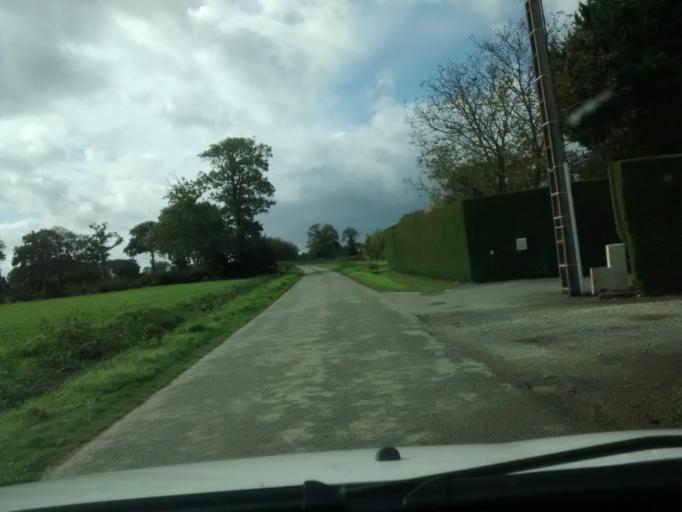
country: FR
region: Brittany
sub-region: Departement d'Ille-et-Vilaine
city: Montreuil-sous-Perouse
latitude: 48.1532
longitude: -1.2939
